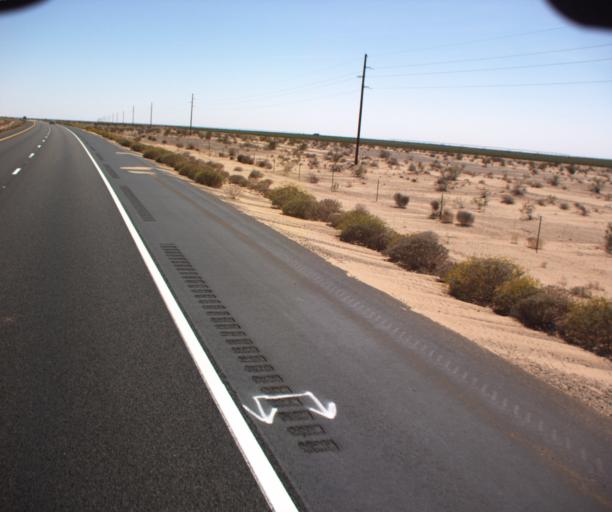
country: US
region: Arizona
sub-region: Yuma County
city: Somerton
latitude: 32.5209
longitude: -114.5621
